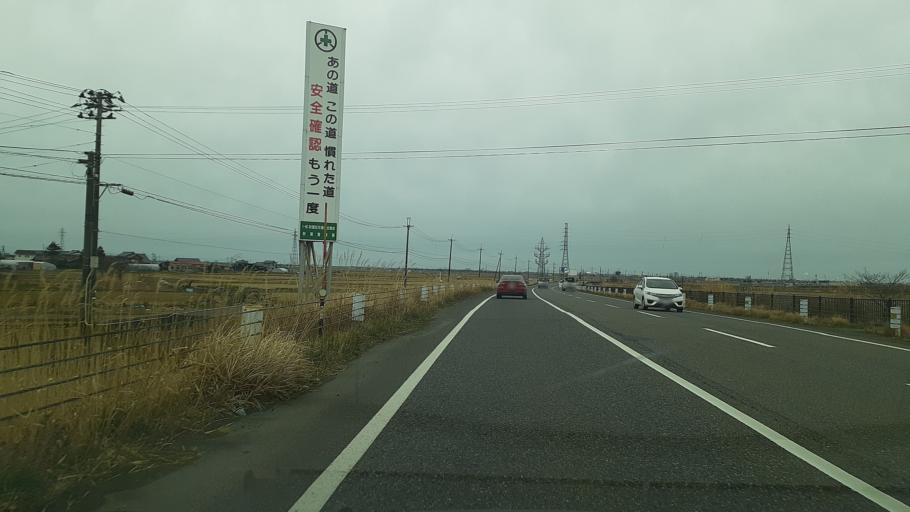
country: JP
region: Niigata
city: Niitsu-honcho
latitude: 37.7991
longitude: 139.1048
